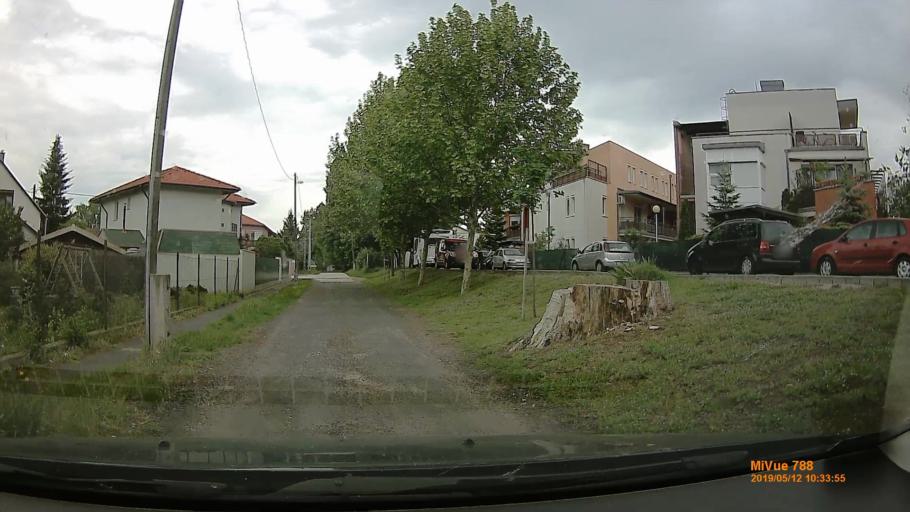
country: HU
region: Budapest
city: Budapest XVII. keruelet
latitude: 47.4826
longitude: 19.2254
